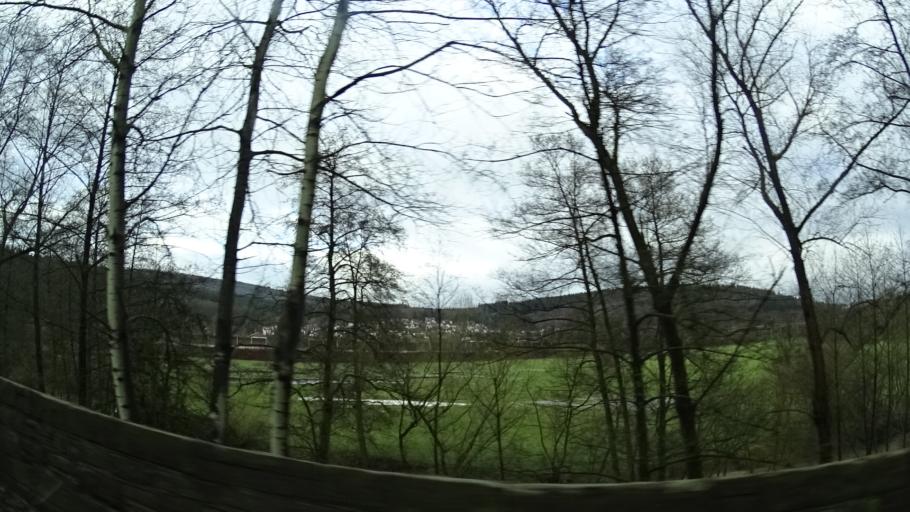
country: DE
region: Hesse
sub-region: Regierungsbezirk Darmstadt
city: Wachtersbach
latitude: 50.2218
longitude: 9.2529
